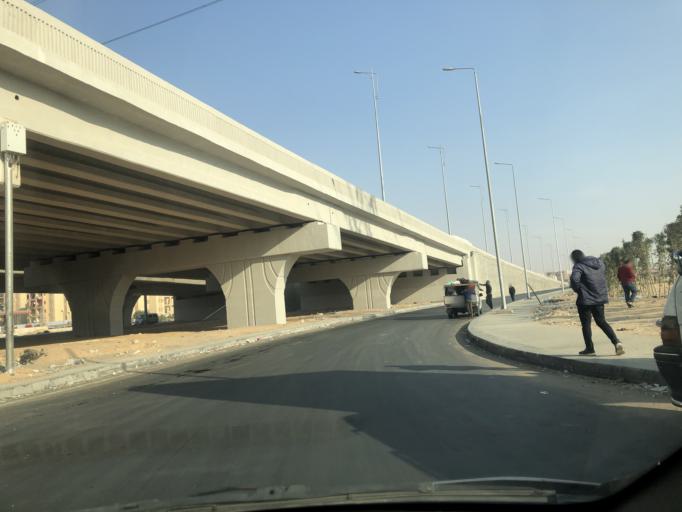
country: EG
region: Al Jizah
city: Madinat Sittah Uktubar
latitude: 29.9106
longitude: 30.9314
